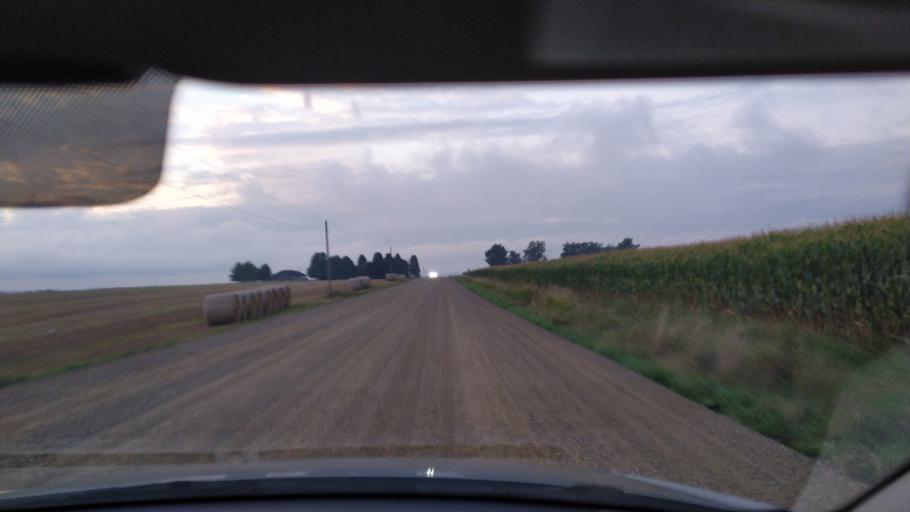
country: CA
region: Ontario
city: Kitchener
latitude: 43.3138
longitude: -80.6128
